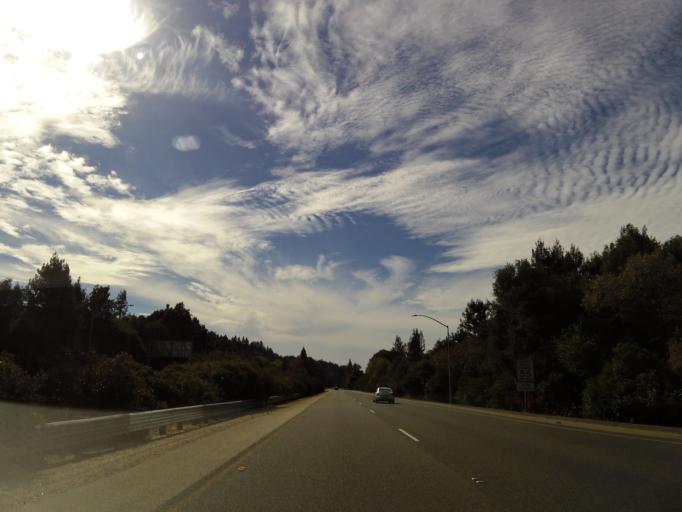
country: US
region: California
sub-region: Santa Cruz County
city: Scotts Valley
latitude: 37.0607
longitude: -122.0049
